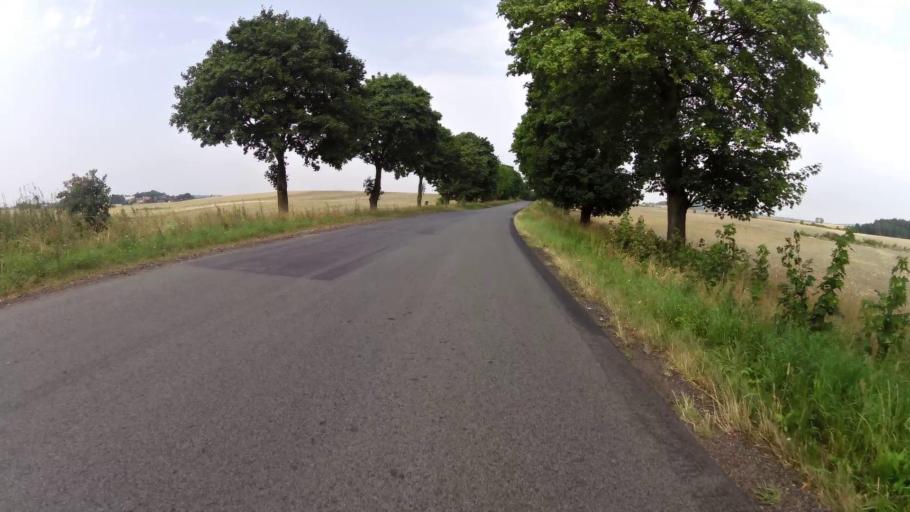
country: PL
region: West Pomeranian Voivodeship
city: Trzcinsko Zdroj
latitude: 52.9448
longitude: 14.6395
